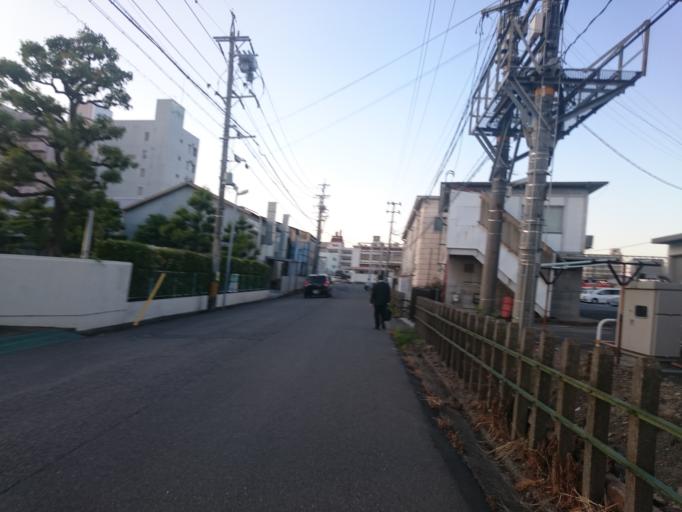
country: JP
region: Mie
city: Yokkaichi
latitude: 34.9617
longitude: 136.6290
